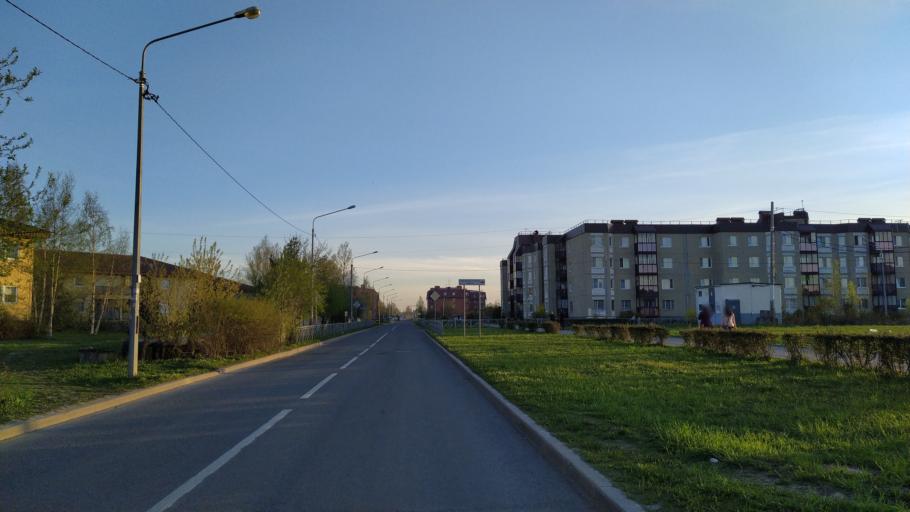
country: RU
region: St.-Petersburg
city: Pushkin
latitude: 59.7034
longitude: 30.3852
